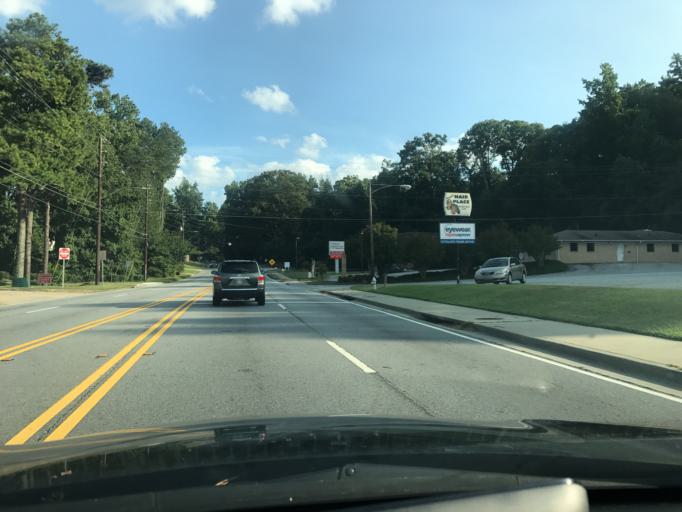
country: US
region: Georgia
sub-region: DeKalb County
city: North Druid Hills
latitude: 33.8363
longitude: -84.3116
